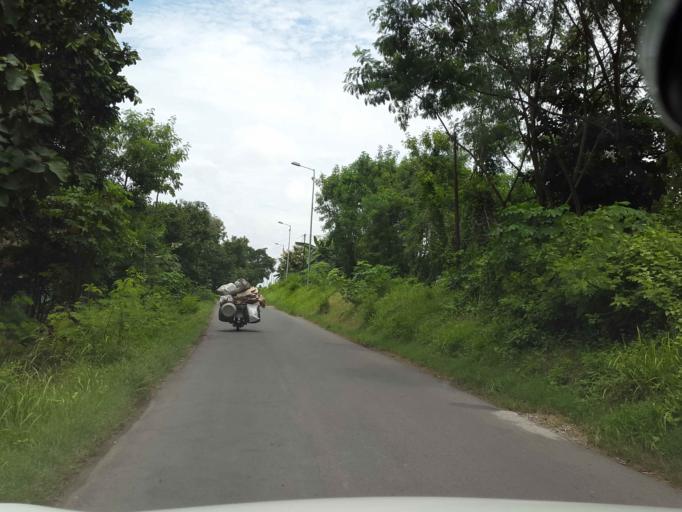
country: ID
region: East Java
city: Mojokerto
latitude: -7.4582
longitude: 112.4154
